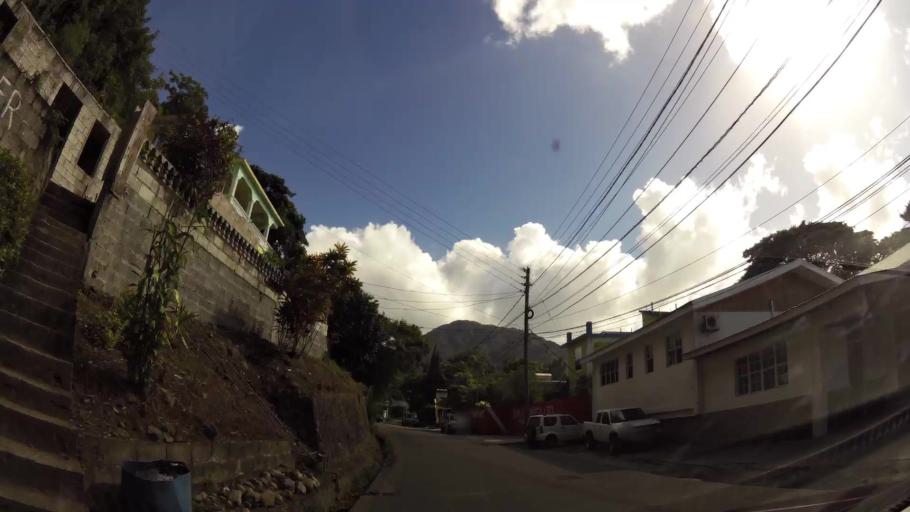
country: DM
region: Saint George
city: Roseau
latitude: 15.2859
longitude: -61.3754
